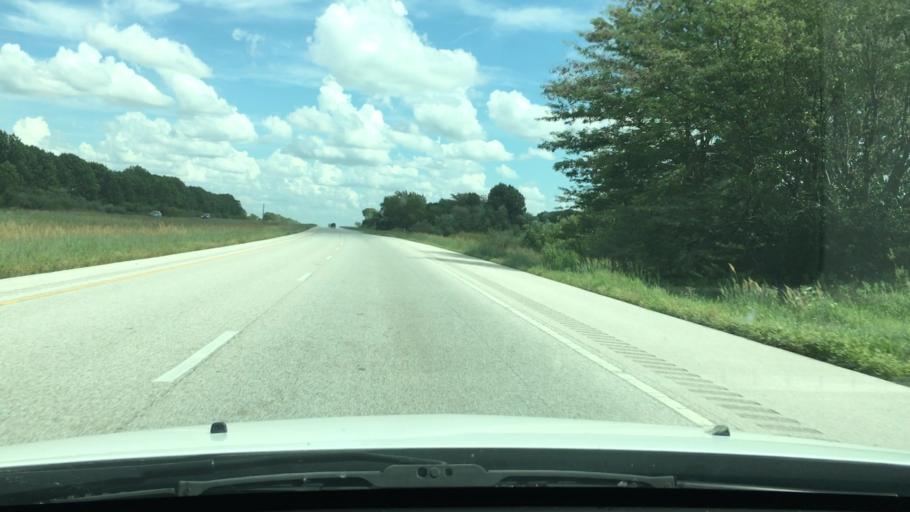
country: US
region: Illinois
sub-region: Scott County
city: Winchester
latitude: 39.6801
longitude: -90.3852
